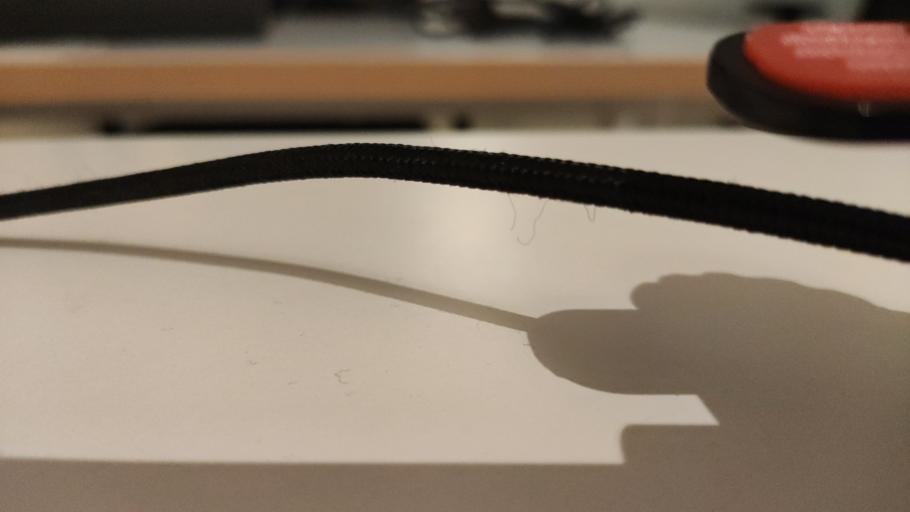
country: RU
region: Moskovskaya
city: Novoye
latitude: 55.6448
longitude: 38.9292
